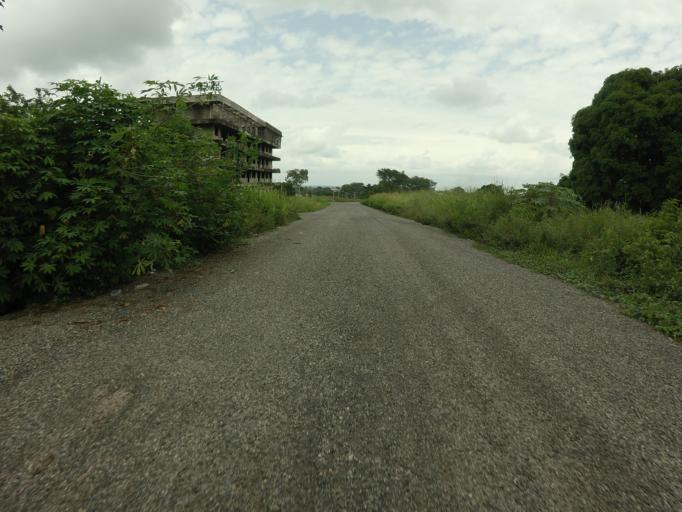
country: GH
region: Volta
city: Ho
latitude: 6.5906
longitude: 0.4639
